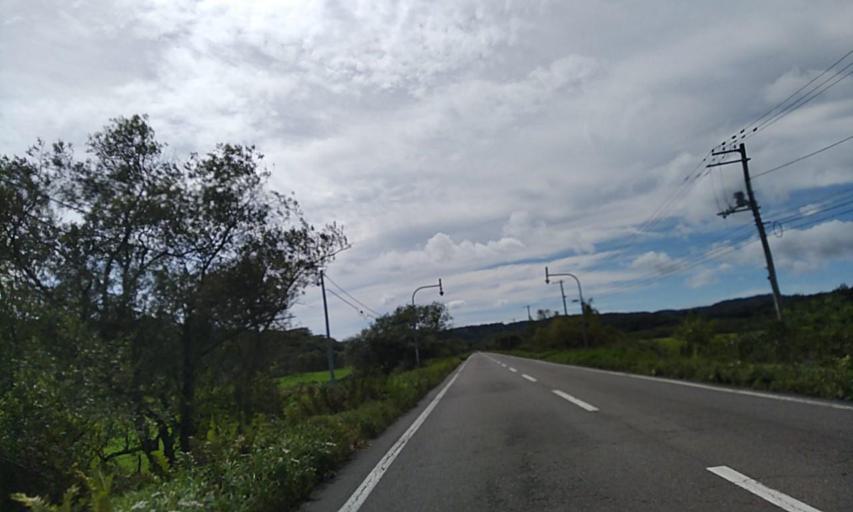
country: JP
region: Hokkaido
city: Kushiro
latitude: 42.8487
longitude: 143.8507
